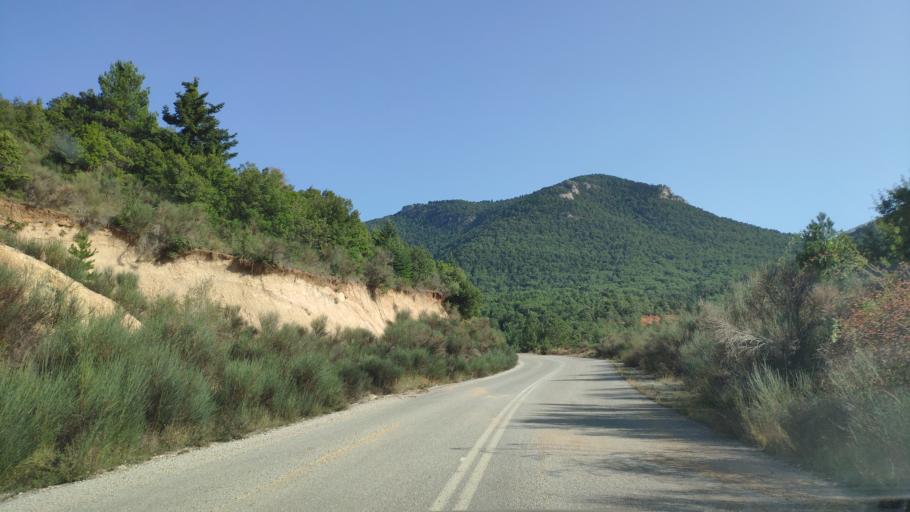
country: GR
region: West Greece
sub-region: Nomos Achaias
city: Aiyira
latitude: 37.9980
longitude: 22.3762
